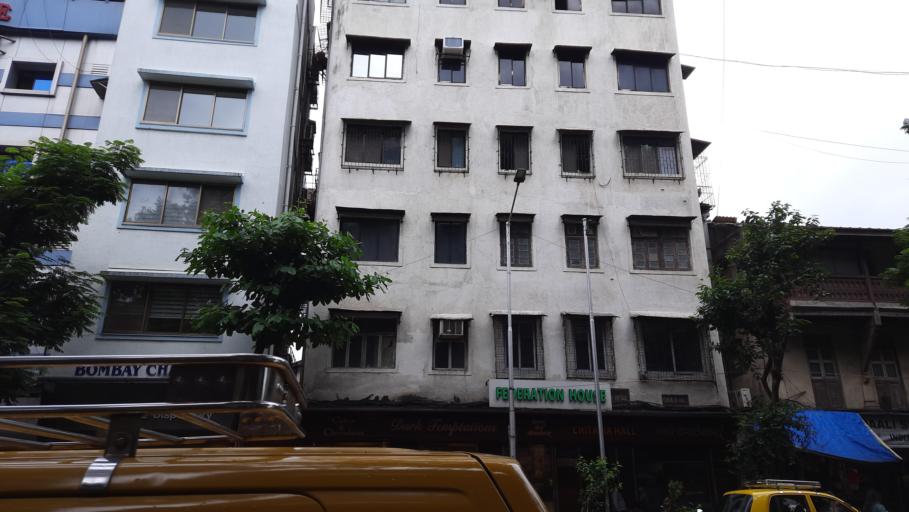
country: IN
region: Maharashtra
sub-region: Raigarh
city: Uran
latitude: 18.9429
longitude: 72.8280
